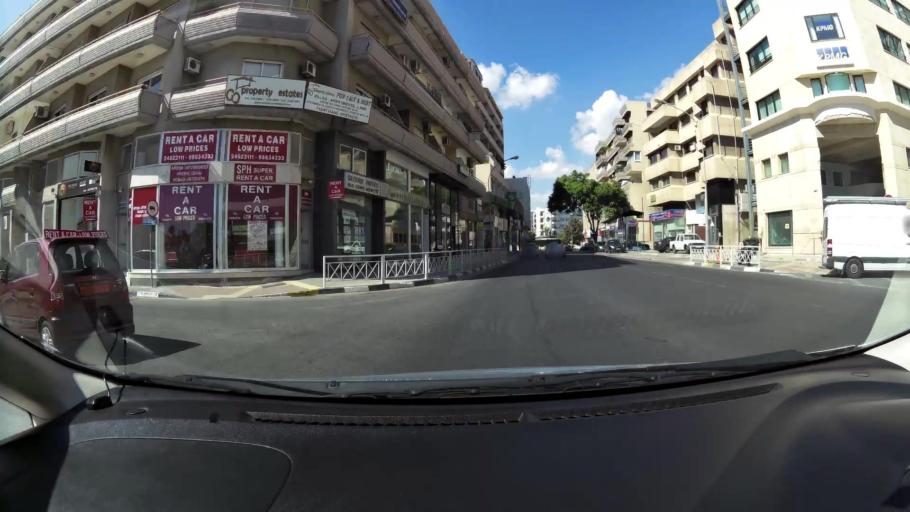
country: CY
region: Larnaka
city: Larnaca
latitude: 34.9176
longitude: 33.6361
